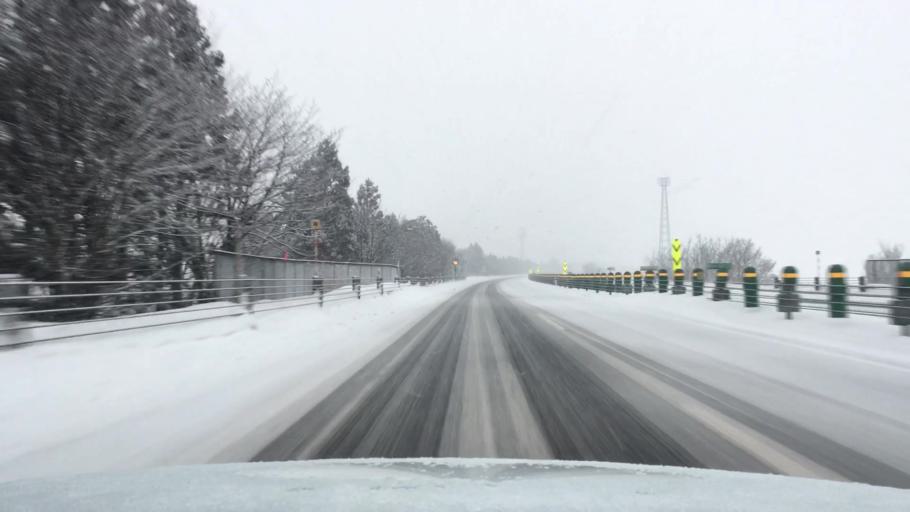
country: JP
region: Akita
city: Hanawa
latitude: 40.2182
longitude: 140.7946
